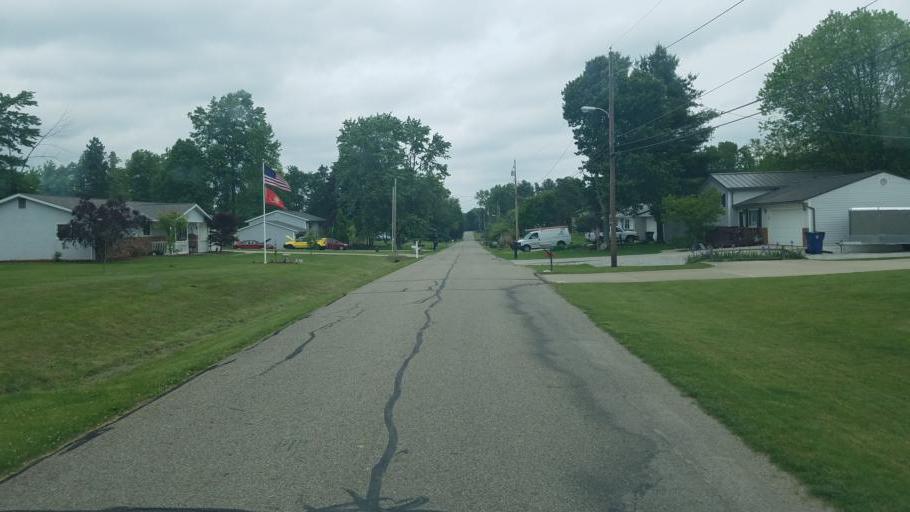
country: US
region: Ohio
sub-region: Licking County
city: Granville South
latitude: 40.0324
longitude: -82.5805
